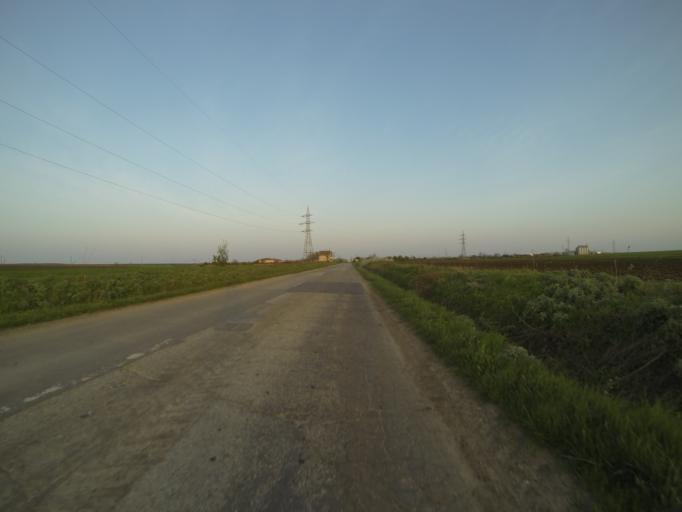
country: RO
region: Dolj
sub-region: Comuna Dranicu
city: Dranic
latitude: 44.0599
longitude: 23.8263
